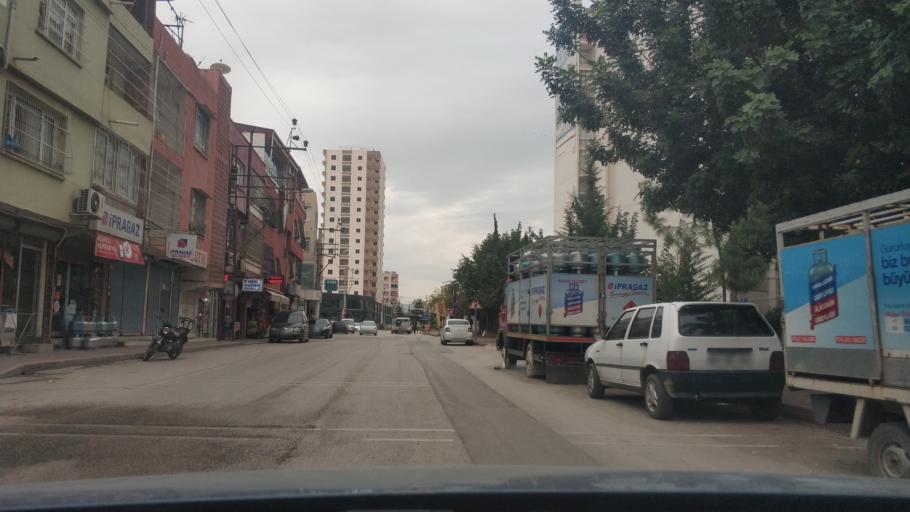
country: TR
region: Adana
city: Yuregir
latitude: 37.0057
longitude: 35.3606
